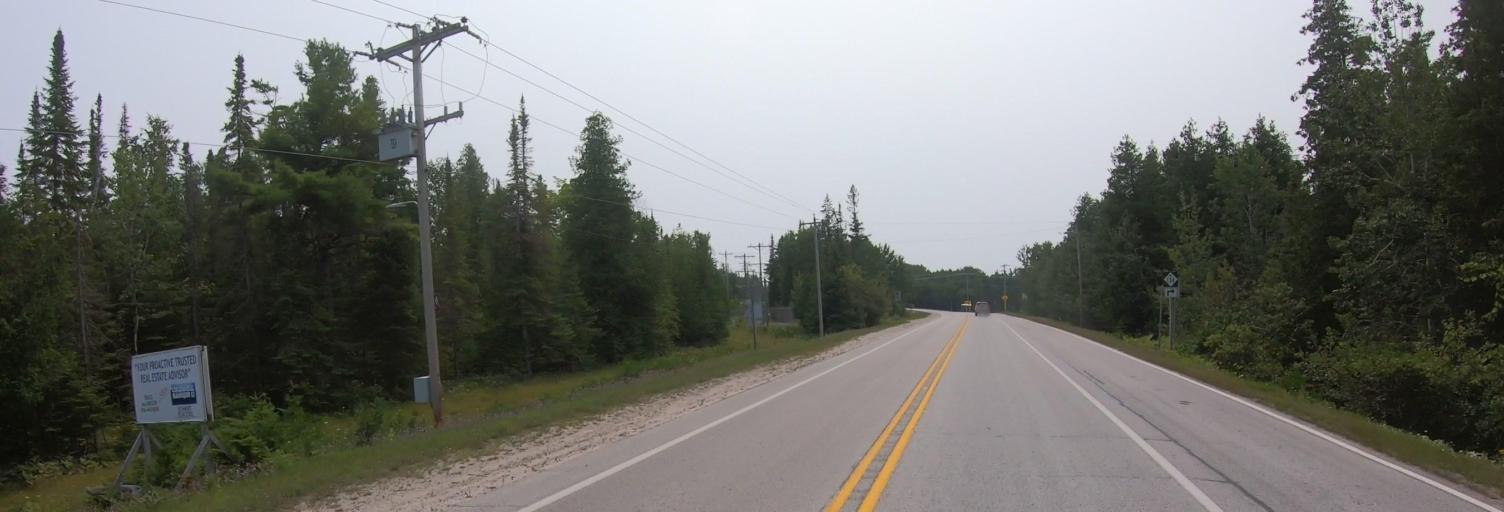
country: CA
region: Ontario
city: Thessalon
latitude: 45.9900
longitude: -83.8759
